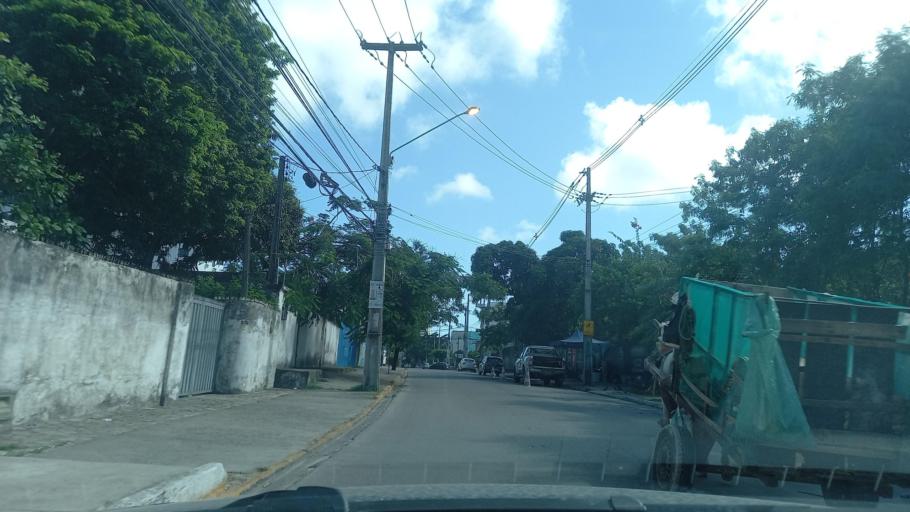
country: BR
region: Pernambuco
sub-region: Jaboatao Dos Guararapes
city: Jaboatao
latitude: -8.1937
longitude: -34.9222
